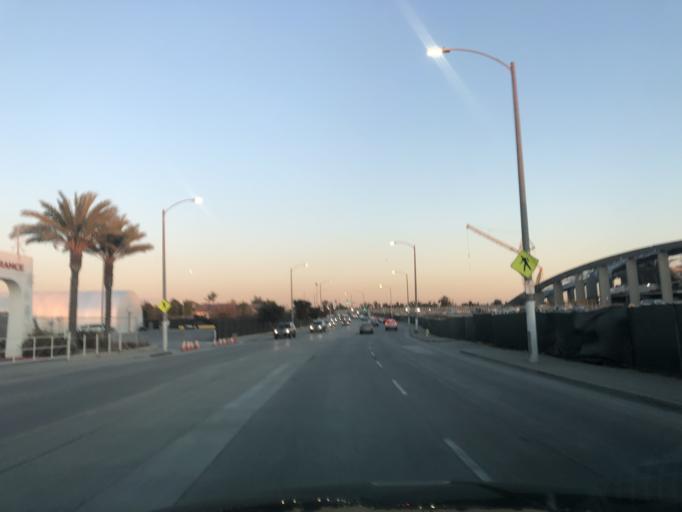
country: US
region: California
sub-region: Los Angeles County
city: Inglewood
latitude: 33.9567
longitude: -118.3427
